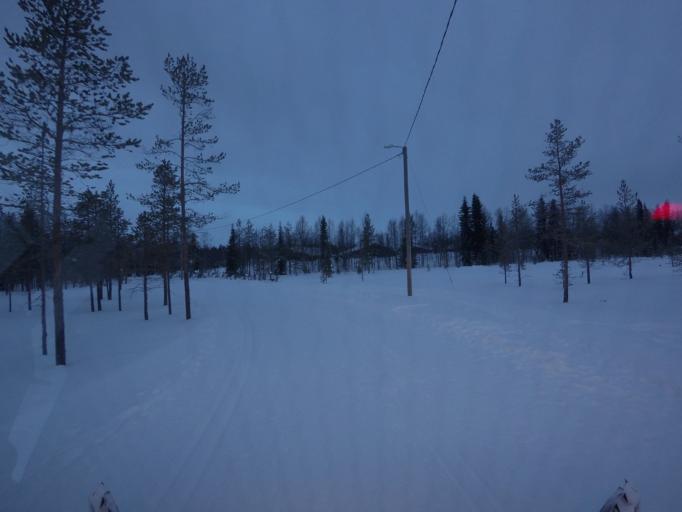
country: FI
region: Lapland
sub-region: Tunturi-Lappi
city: Kolari
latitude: 67.6155
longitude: 24.1635
